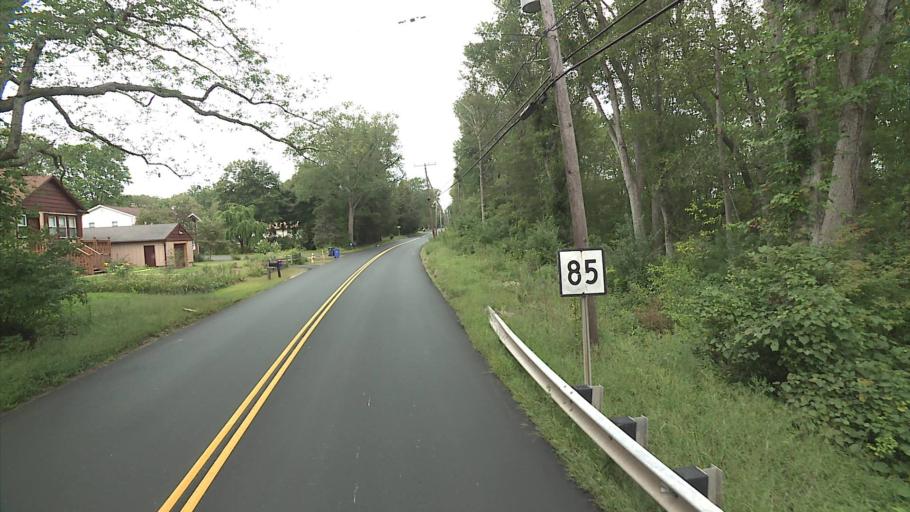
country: US
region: Connecticut
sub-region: New London County
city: Colchester
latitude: 41.5847
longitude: -72.3374
